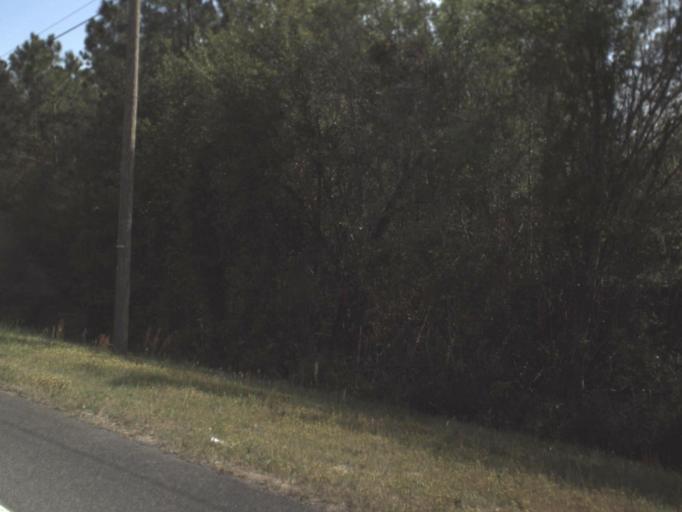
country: US
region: Florida
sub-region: Santa Rosa County
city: East Milton
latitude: 30.5852
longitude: -86.9315
